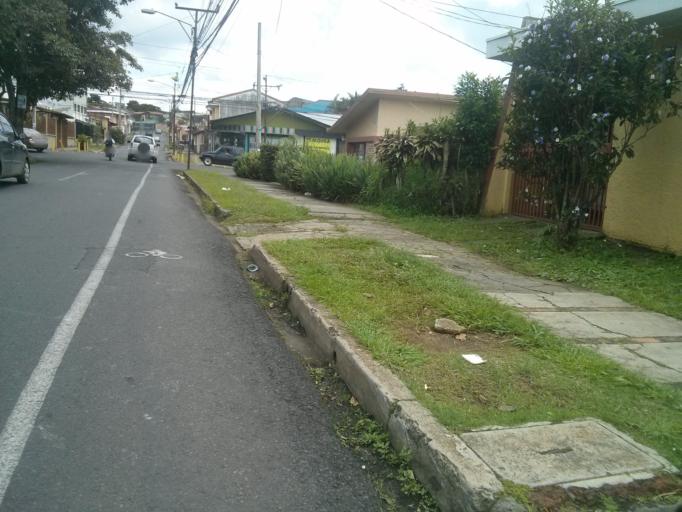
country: CR
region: San Jose
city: San Pedro
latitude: 9.9296
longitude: -84.0493
